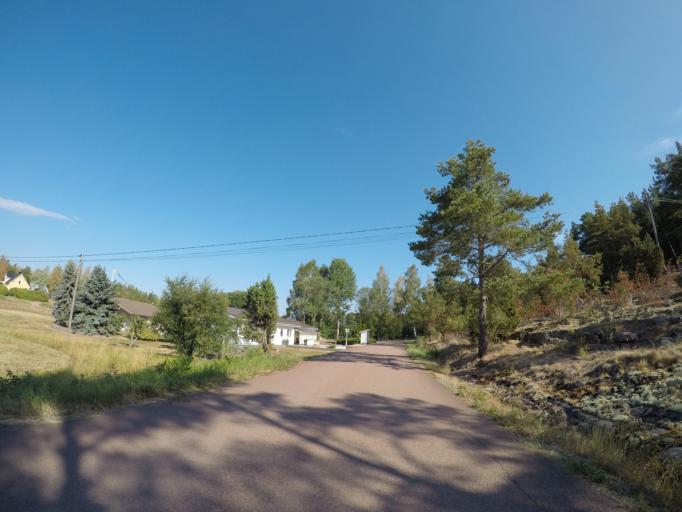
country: AX
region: Alands landsbygd
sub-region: Finstroem
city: Finstroem
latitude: 60.3333
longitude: 19.9109
